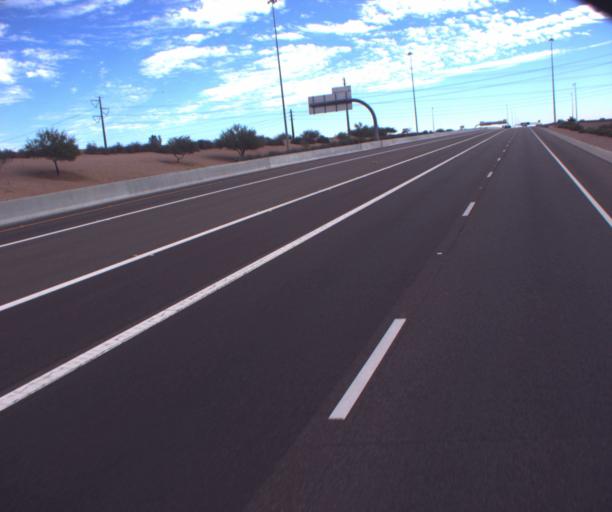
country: US
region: Arizona
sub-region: Maricopa County
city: Guadalupe
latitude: 33.2960
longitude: -111.9666
